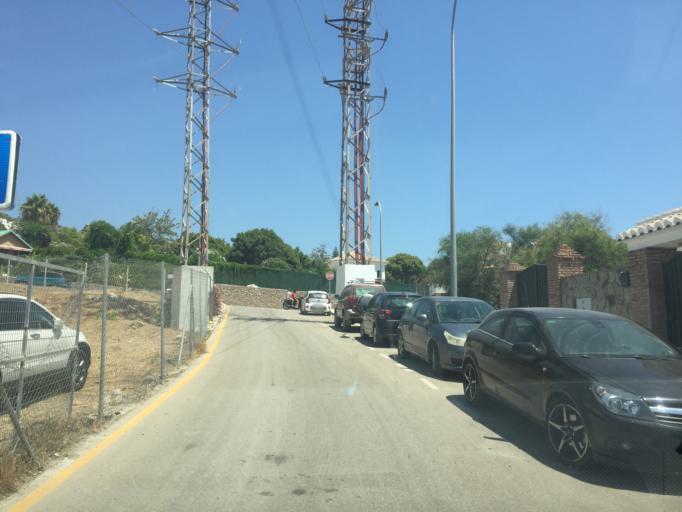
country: ES
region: Andalusia
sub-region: Provincia de Malaga
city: Nerja
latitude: 36.7642
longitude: -3.8720
